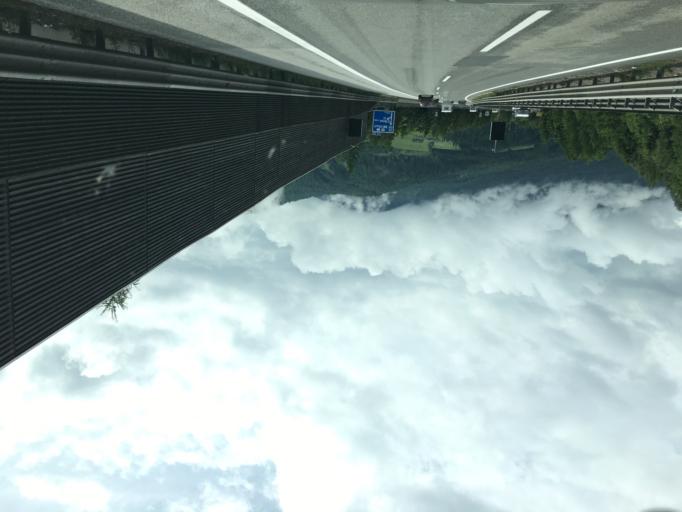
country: AT
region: Salzburg
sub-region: Politischer Bezirk Tamsweg
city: Sankt Michael im Lungau
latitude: 47.1014
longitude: 13.5996
